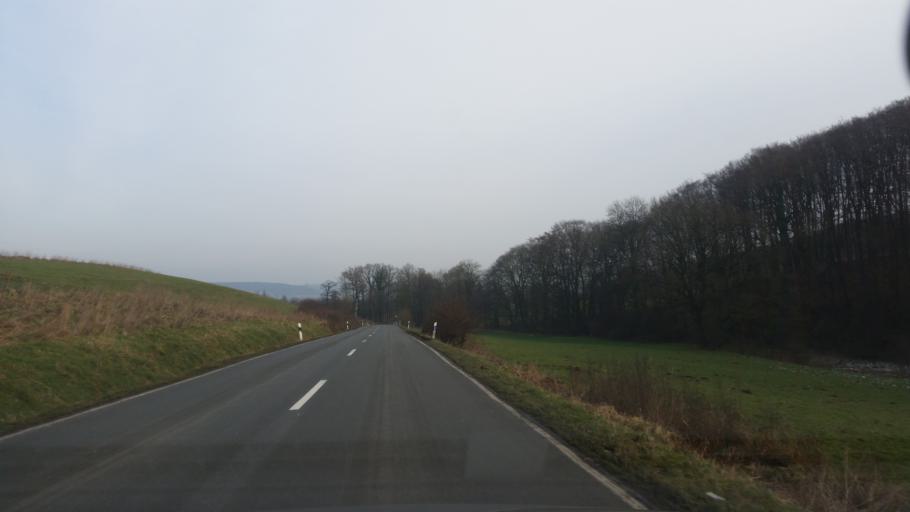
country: DE
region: North Rhine-Westphalia
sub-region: Regierungsbezirk Detmold
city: Barntrup
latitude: 52.0647
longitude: 9.1682
